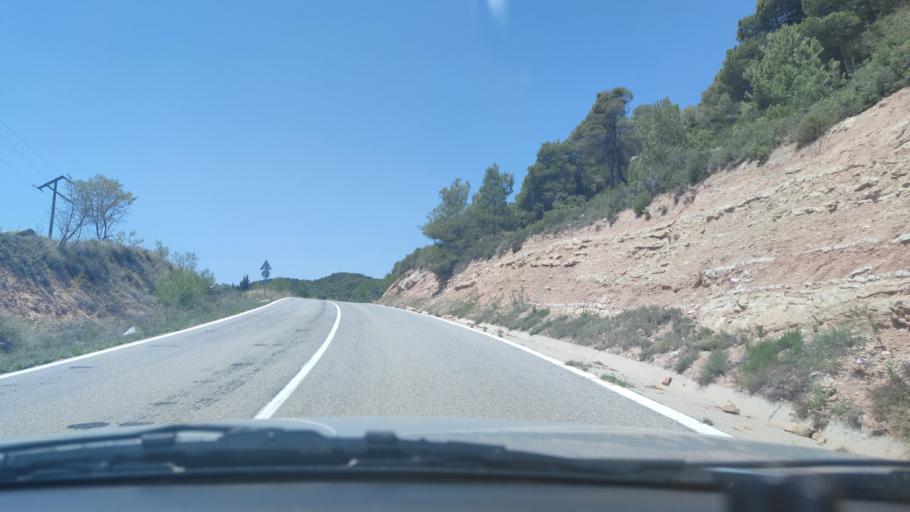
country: ES
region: Catalonia
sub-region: Provincia de Tarragona
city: Vimbodi
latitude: 41.4255
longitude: 1.0262
